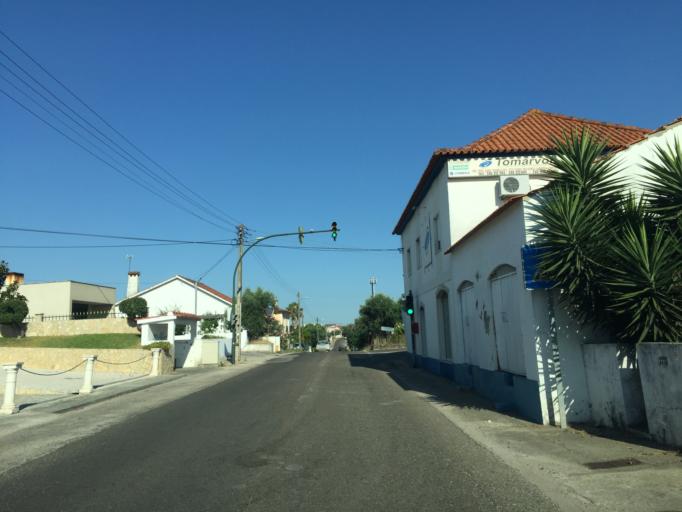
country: PT
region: Santarem
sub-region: Tomar
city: Tomar
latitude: 39.5953
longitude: -8.3719
